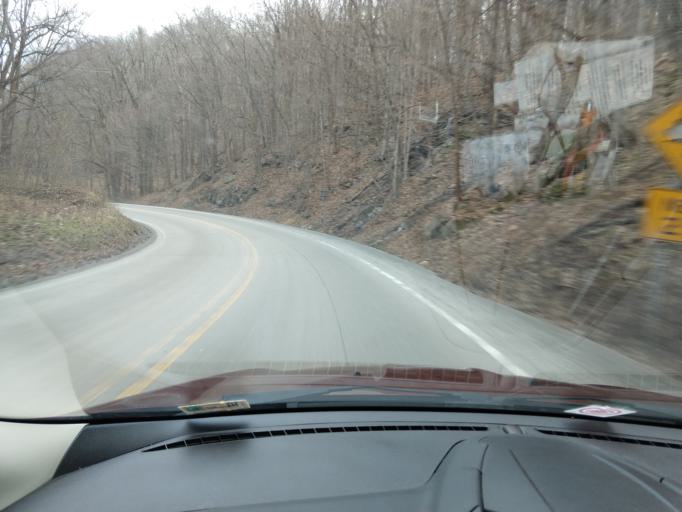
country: US
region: West Virginia
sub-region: Randolph County
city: Elkins
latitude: 38.6549
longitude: -79.9209
